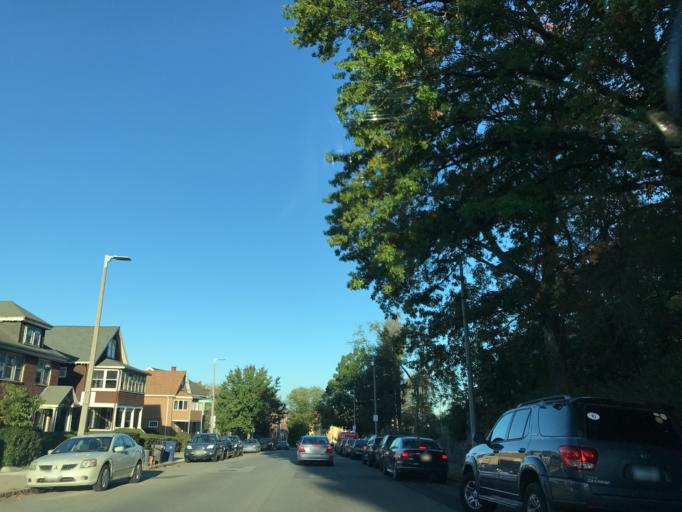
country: US
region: Massachusetts
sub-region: Norfolk County
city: Brookline
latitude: 42.3465
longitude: -71.1471
